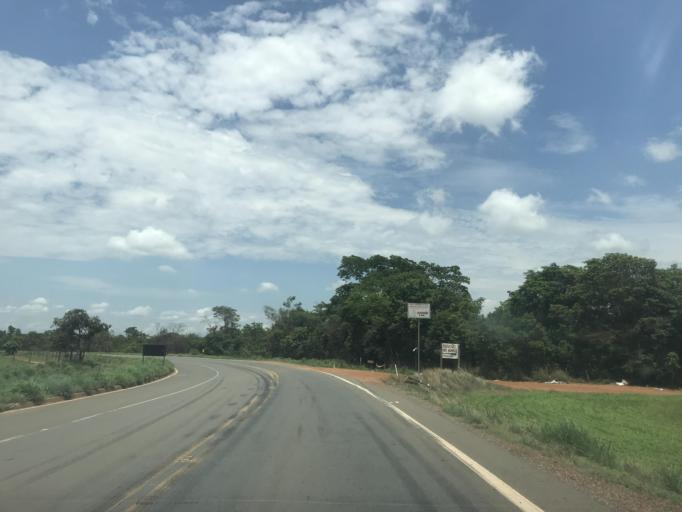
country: BR
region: Goias
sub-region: Luziania
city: Luziania
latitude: -16.3899
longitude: -48.1616
